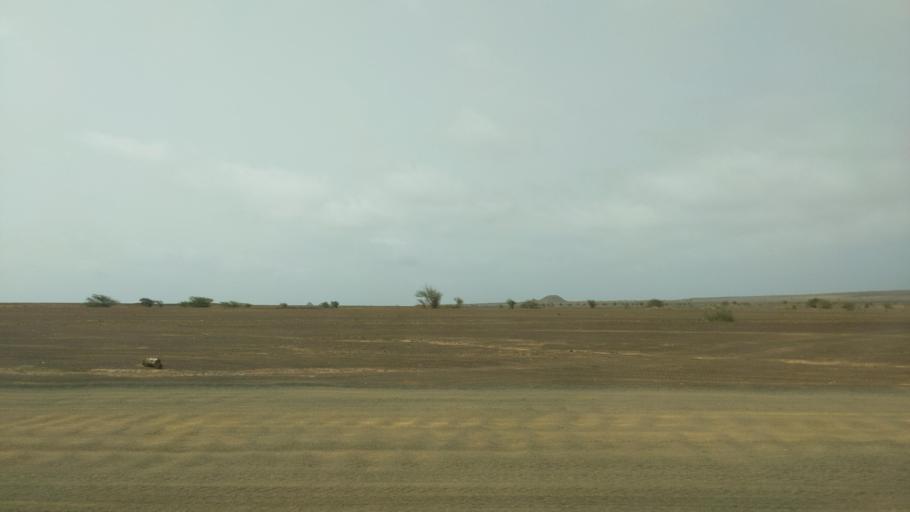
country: CV
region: Sal
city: Espargos
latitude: 16.7974
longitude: -22.9564
